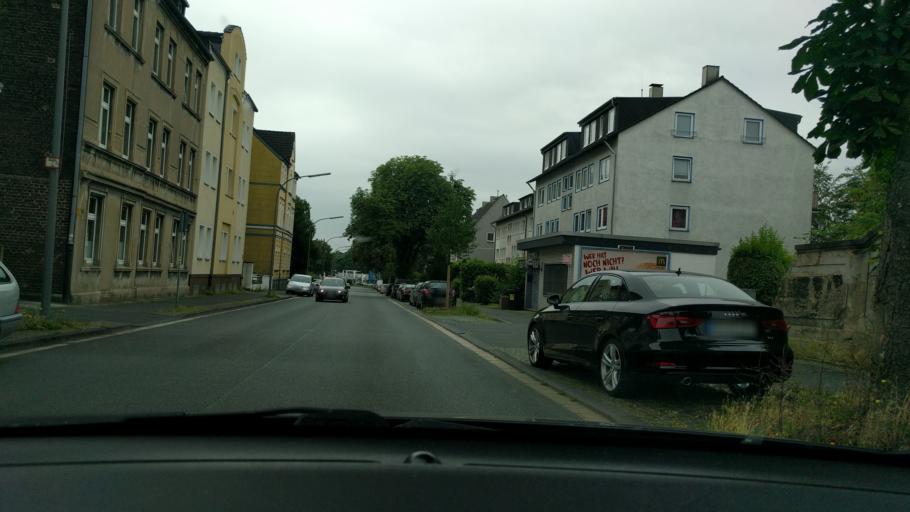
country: DE
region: North Rhine-Westphalia
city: Witten
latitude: 51.4723
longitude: 7.2977
